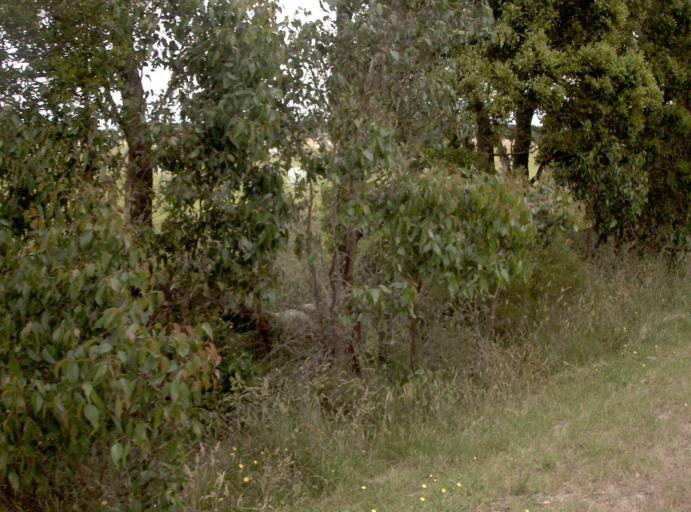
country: AU
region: Victoria
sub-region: Latrobe
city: Traralgon
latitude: -38.4900
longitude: 146.8194
